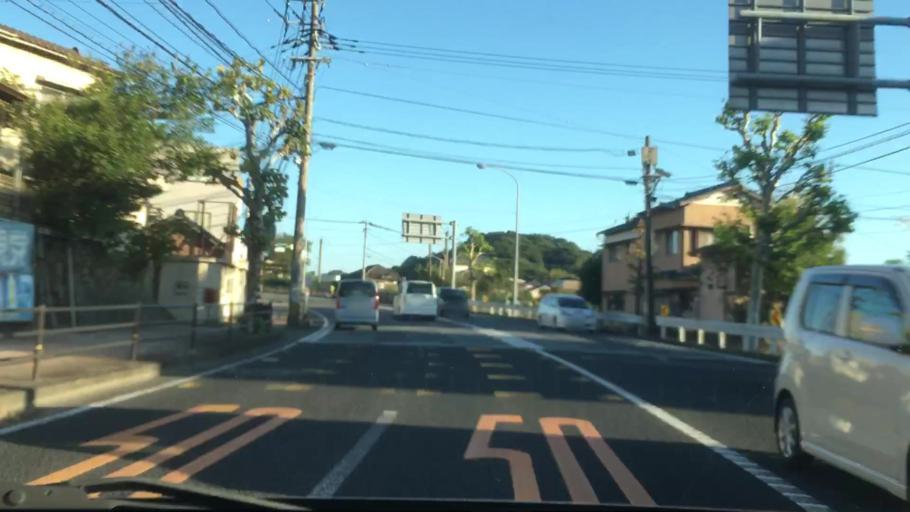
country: JP
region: Nagasaki
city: Sasebo
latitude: 33.1569
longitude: 129.7526
